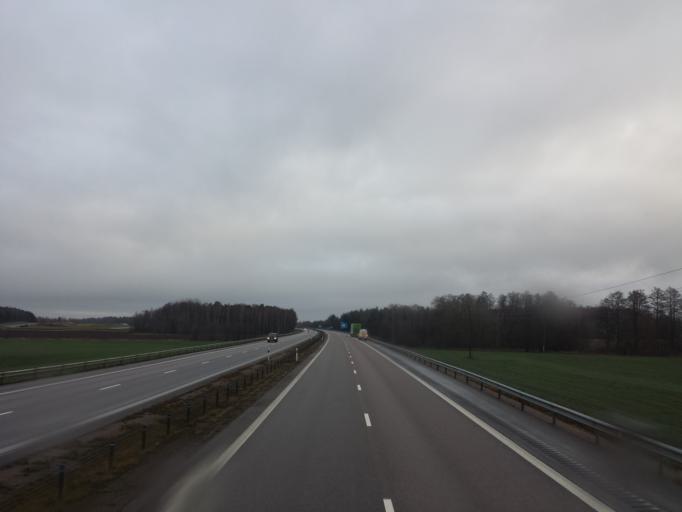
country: SE
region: OEstergoetland
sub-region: Mjolby Kommun
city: Mantorp
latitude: 58.3624
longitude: 15.2664
